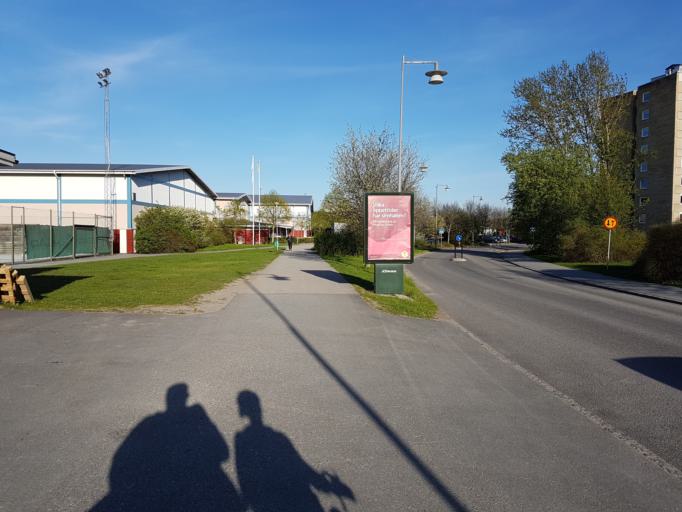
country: SE
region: Stockholm
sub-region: Solna Kommun
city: Rasunda
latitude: 59.3771
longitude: 17.9746
